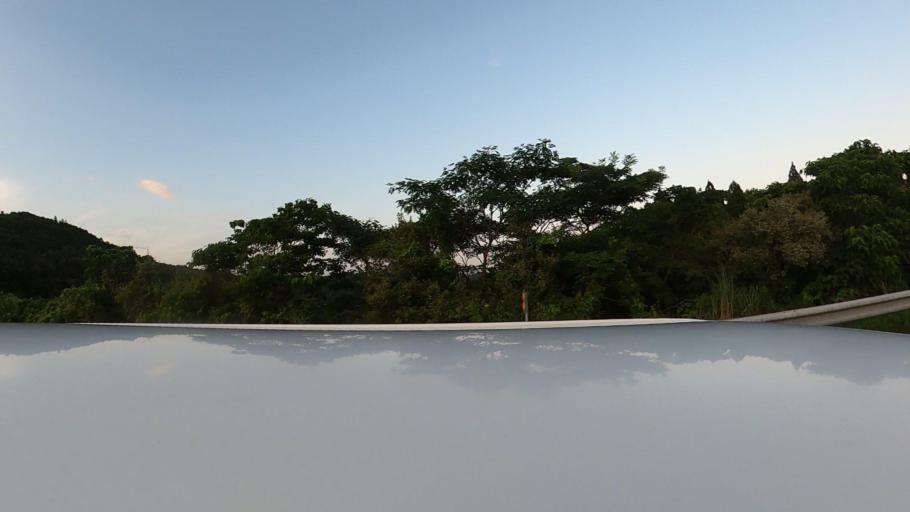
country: JP
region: Miyazaki
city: Nobeoka
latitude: 32.5701
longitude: 131.6231
